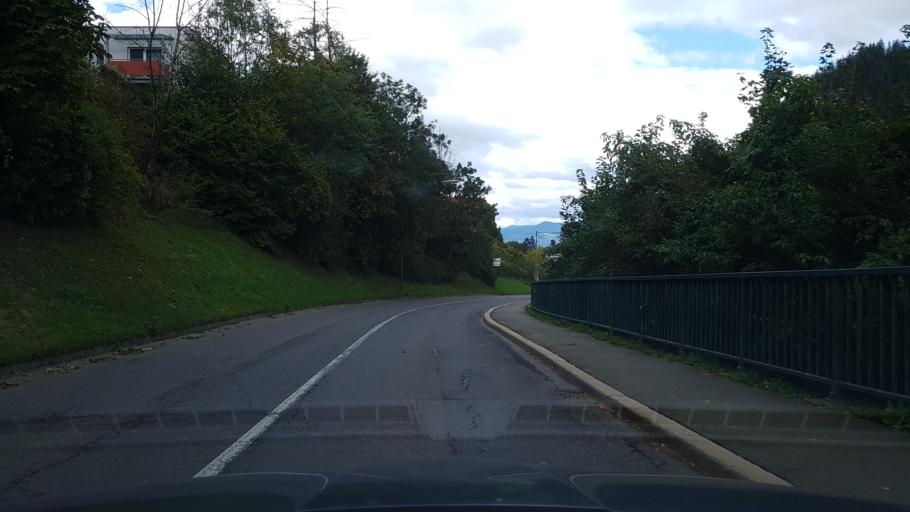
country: AT
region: Styria
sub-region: Politischer Bezirk Murtal
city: Judenburg
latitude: 47.1680
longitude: 14.6649
